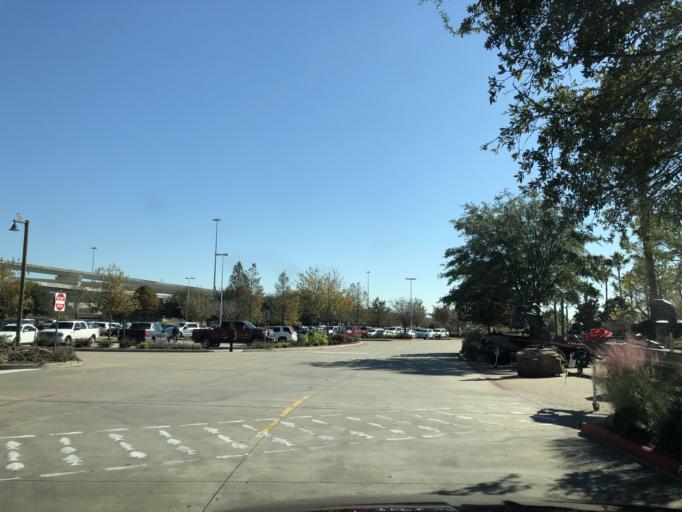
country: US
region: Texas
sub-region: Brazoria County
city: Brookside Village
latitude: 29.5955
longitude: -95.3895
